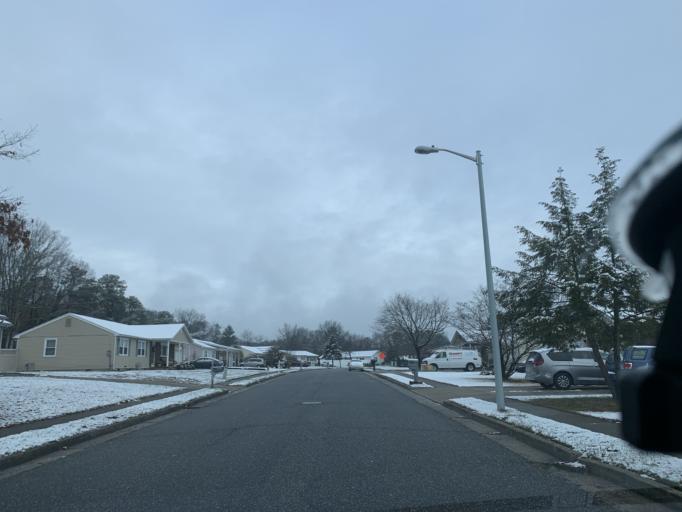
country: US
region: New Jersey
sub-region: Atlantic County
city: Pomona
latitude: 39.4325
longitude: -74.5934
